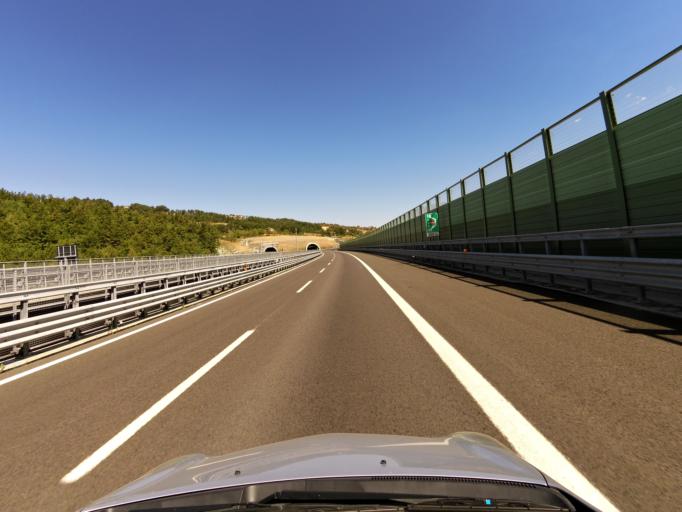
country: IT
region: Emilia-Romagna
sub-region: Provincia di Bologna
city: Castiglione dei Pepoli
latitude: 44.1627
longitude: 11.1971
